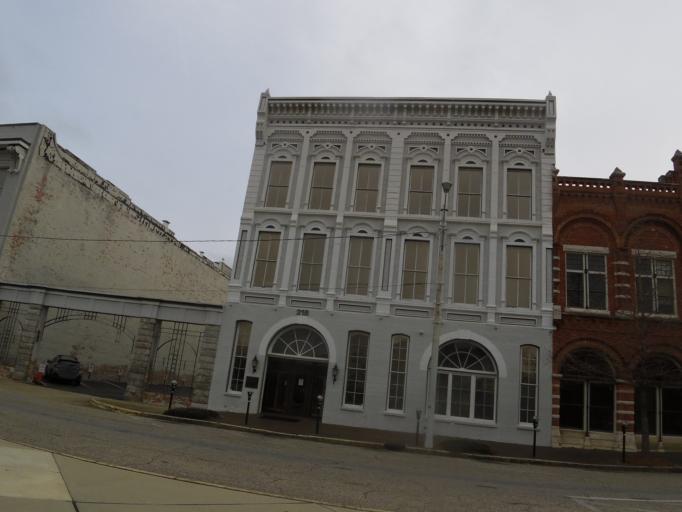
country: US
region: Alabama
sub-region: Montgomery County
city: Montgomery
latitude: 32.3806
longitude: -86.3122
